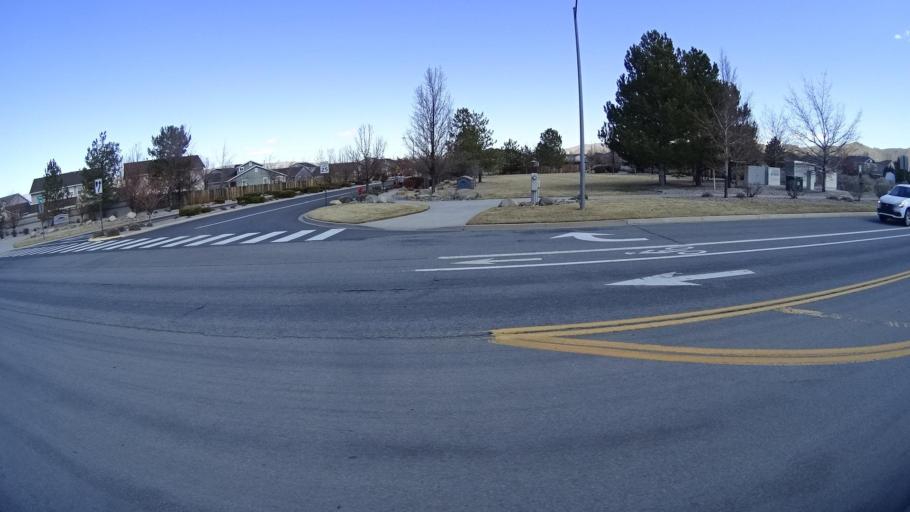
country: US
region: Nevada
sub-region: Washoe County
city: Lemmon Valley
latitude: 39.6379
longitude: -119.8589
